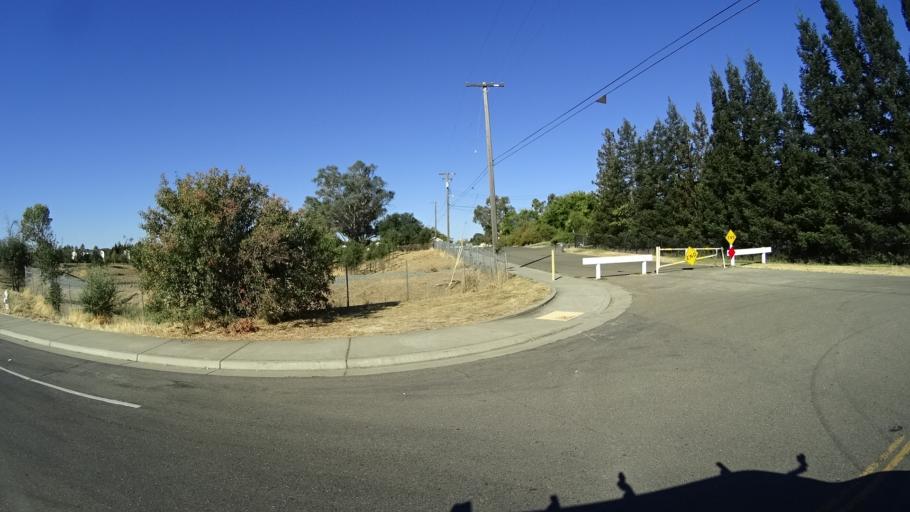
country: US
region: California
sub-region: Sacramento County
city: Vineyard
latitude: 38.4488
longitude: -121.3664
